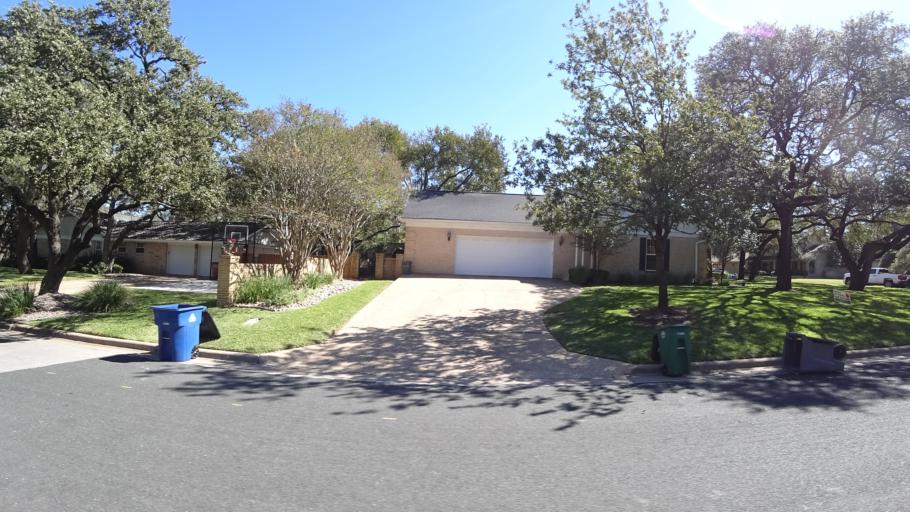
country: US
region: Texas
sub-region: Williamson County
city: Jollyville
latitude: 30.3693
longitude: -97.7665
